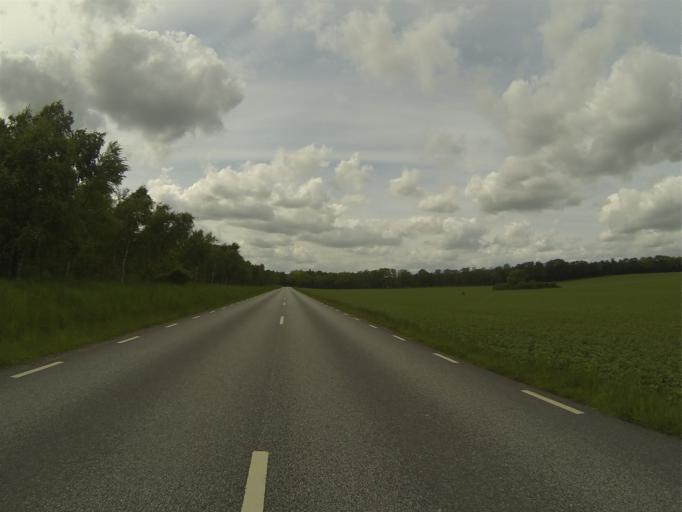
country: SE
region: Skane
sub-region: Sjobo Kommun
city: Sjoebo
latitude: 55.6565
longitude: 13.6920
